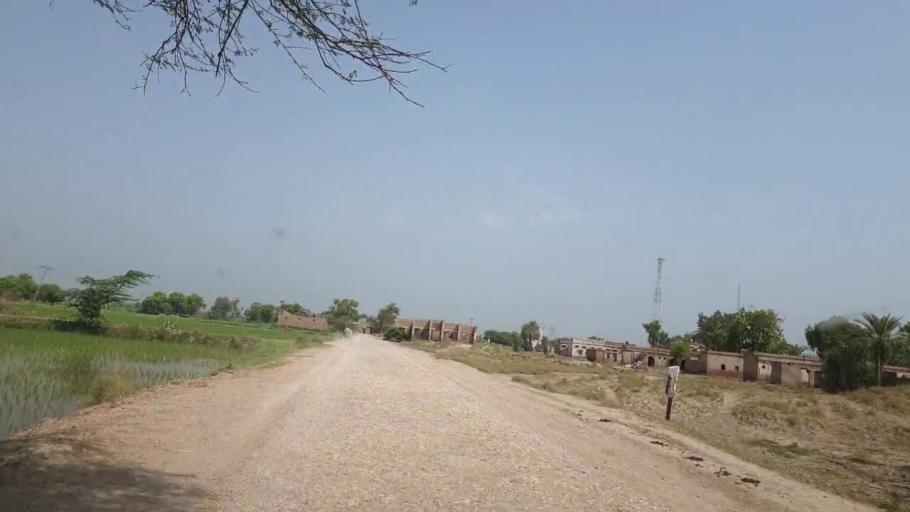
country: PK
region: Sindh
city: Lakhi
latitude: 27.8696
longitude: 68.6609
